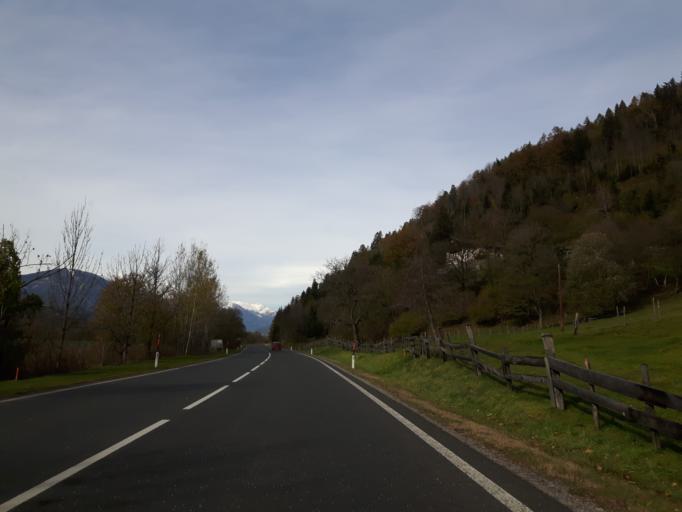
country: AT
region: Tyrol
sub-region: Politischer Bezirk Lienz
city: Lavant
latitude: 46.8030
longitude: 12.8701
